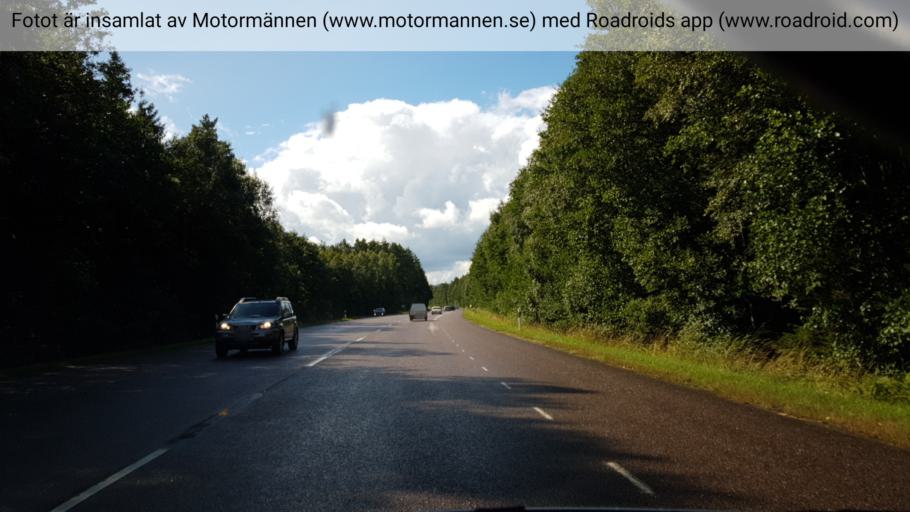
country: SE
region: Vaestra Goetaland
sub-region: Skovde Kommun
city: Stopen
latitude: 58.4244
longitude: 13.9038
